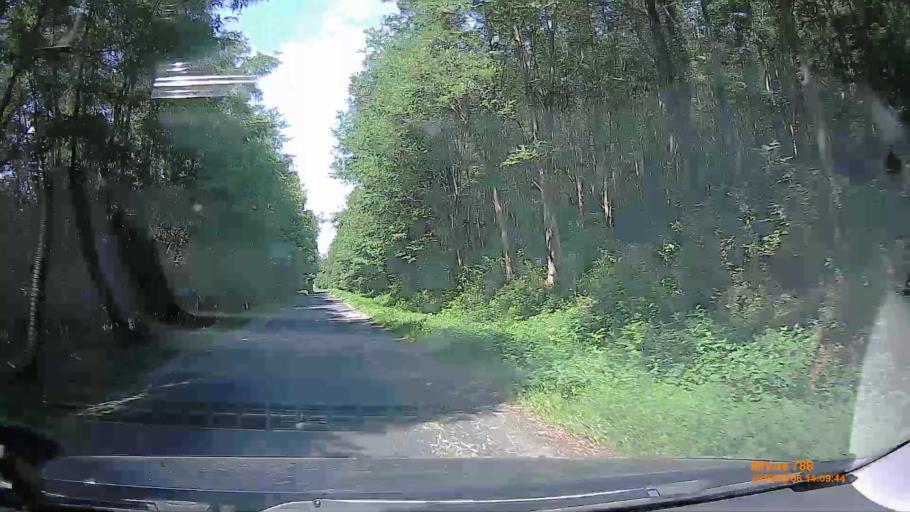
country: HU
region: Zala
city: Zalakomar
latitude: 46.5428
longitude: 17.0826
